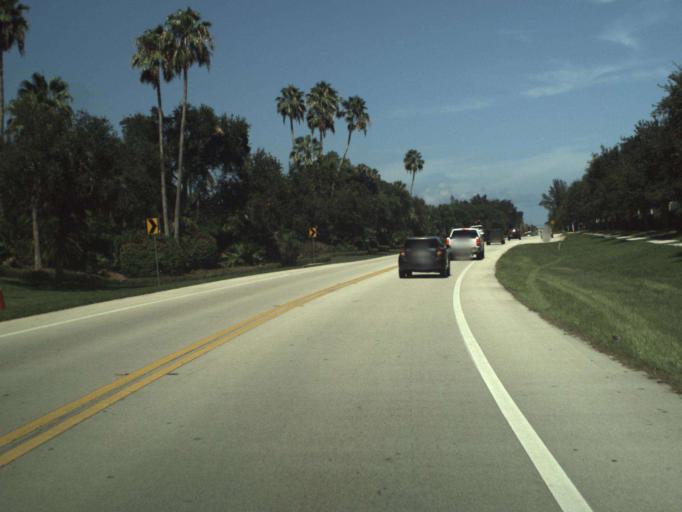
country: US
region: Florida
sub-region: Indian River County
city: Wabasso Beach
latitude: 27.7633
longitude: -80.4122
